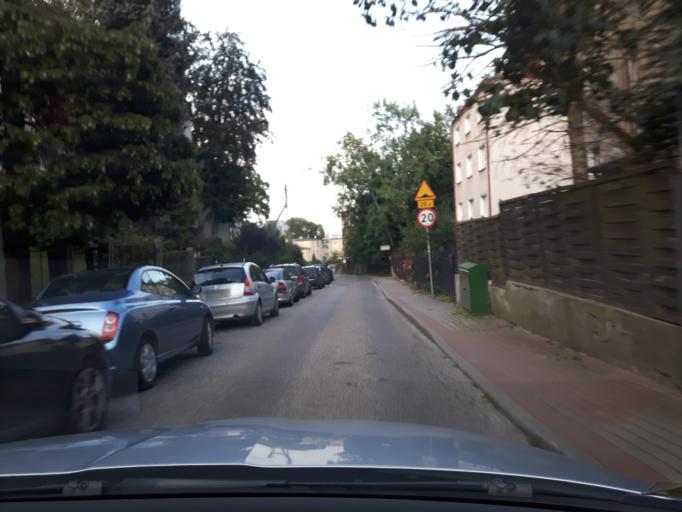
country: PL
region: Pomeranian Voivodeship
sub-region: Gdynia
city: Gdynia
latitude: 54.5129
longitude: 18.5271
